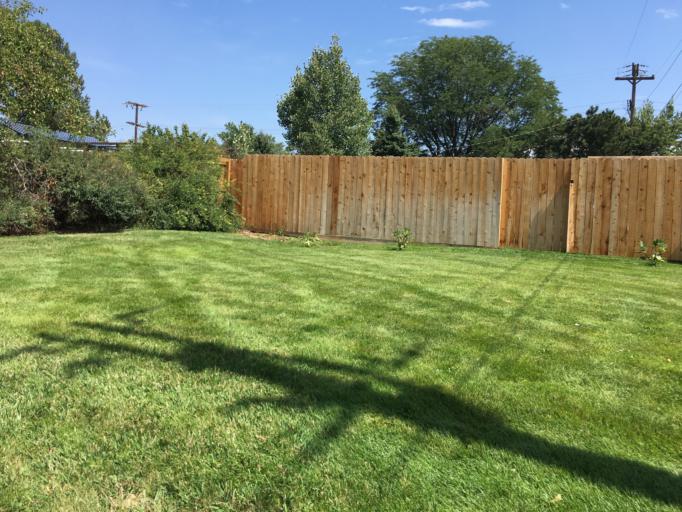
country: US
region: Colorado
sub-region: Arapahoe County
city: Glendale
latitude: 39.6707
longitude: -104.9222
